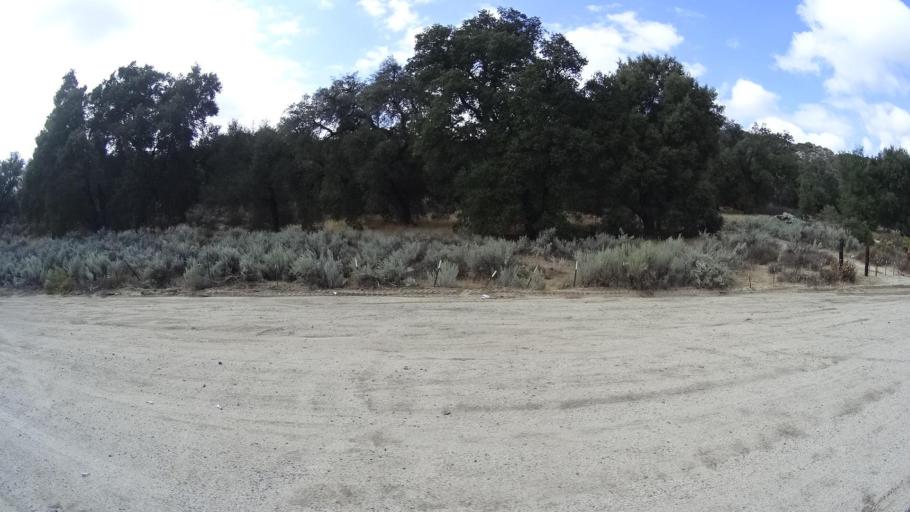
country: US
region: California
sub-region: San Diego County
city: Campo
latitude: 32.7006
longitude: -116.4890
